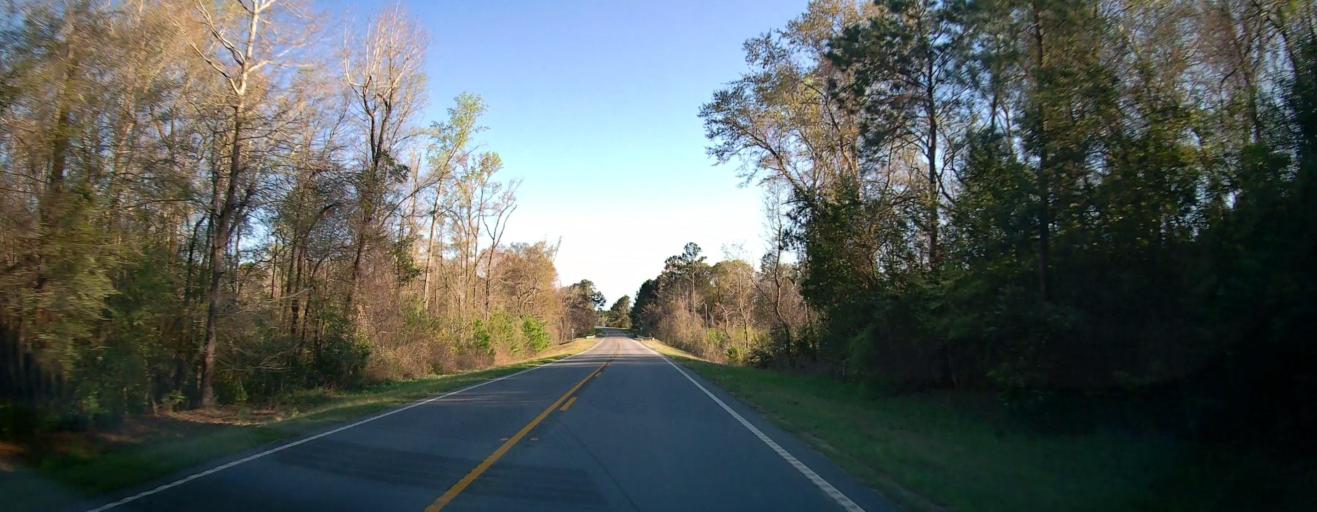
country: US
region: Georgia
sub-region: Pulaski County
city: Hawkinsville
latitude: 32.1941
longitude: -83.3701
